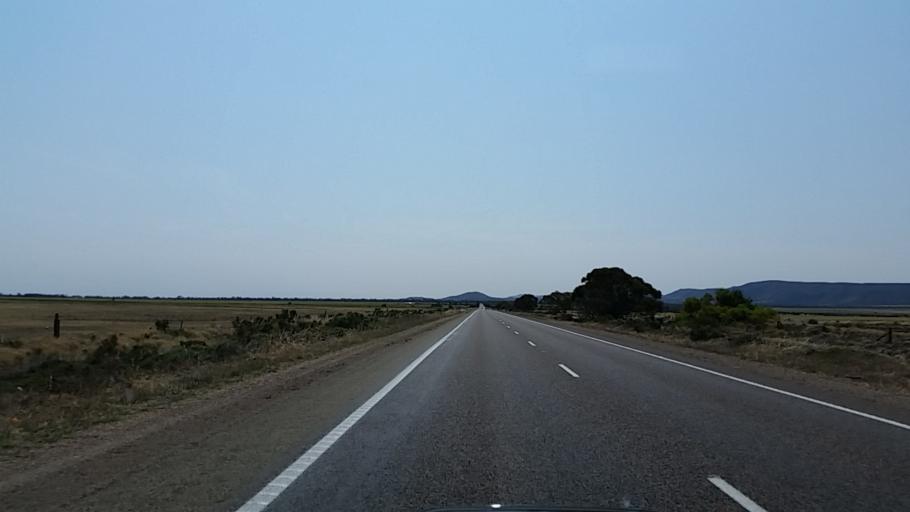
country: AU
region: South Australia
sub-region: Port Pirie City and Dists
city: Port Pirie
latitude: -32.8987
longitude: 137.9823
